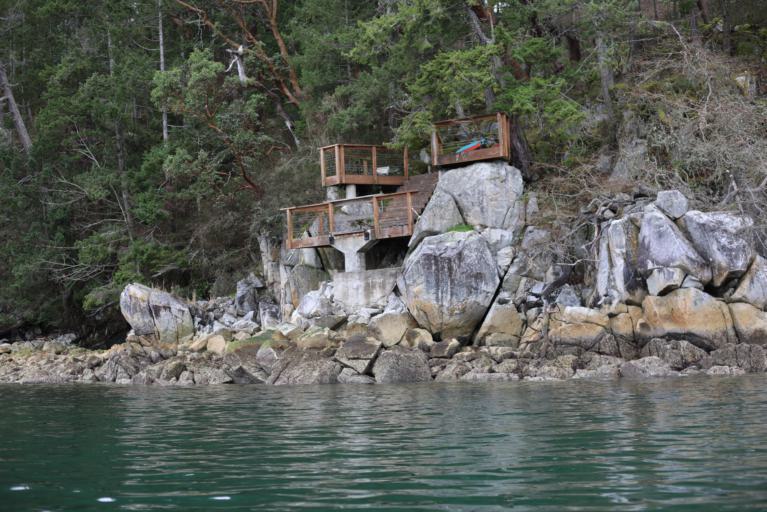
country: CA
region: British Columbia
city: North Saanich
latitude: 48.6611
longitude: -123.5335
